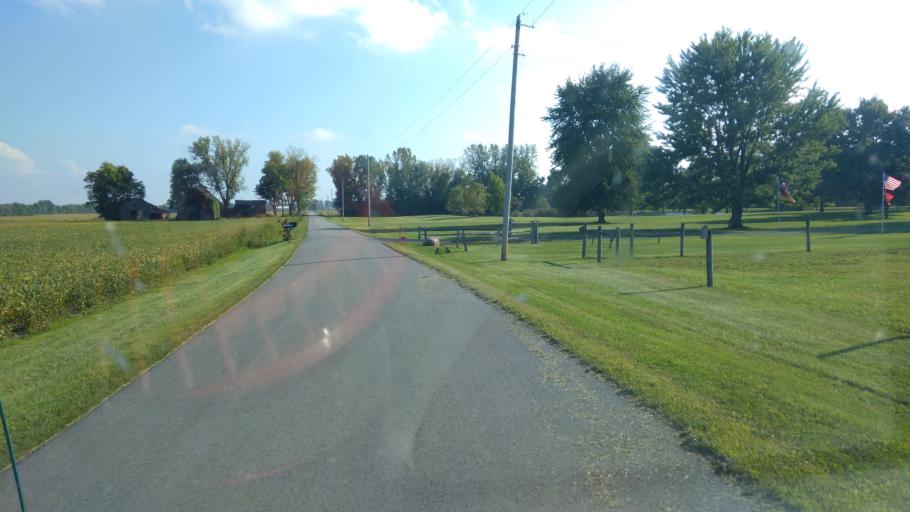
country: US
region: Ohio
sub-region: Hardin County
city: Forest
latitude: 40.7299
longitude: -83.4778
